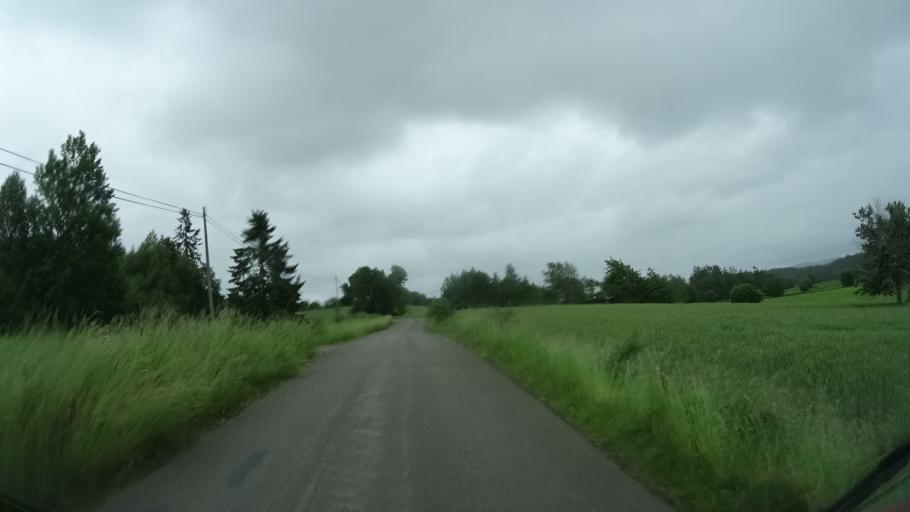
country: SE
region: Joenkoeping
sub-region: Eksjo Kommun
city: Mariannelund
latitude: 57.6826
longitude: 15.5756
